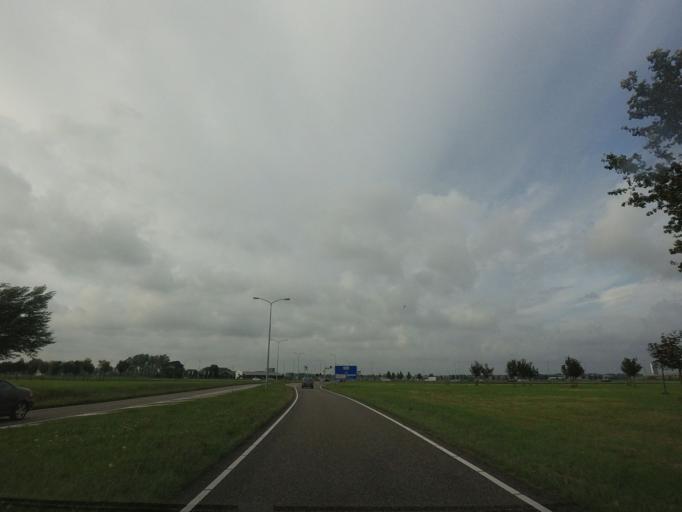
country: NL
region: North Holland
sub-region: Gemeente Haarlemmermeer
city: Hoofddorp
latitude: 52.2785
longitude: 4.6713
